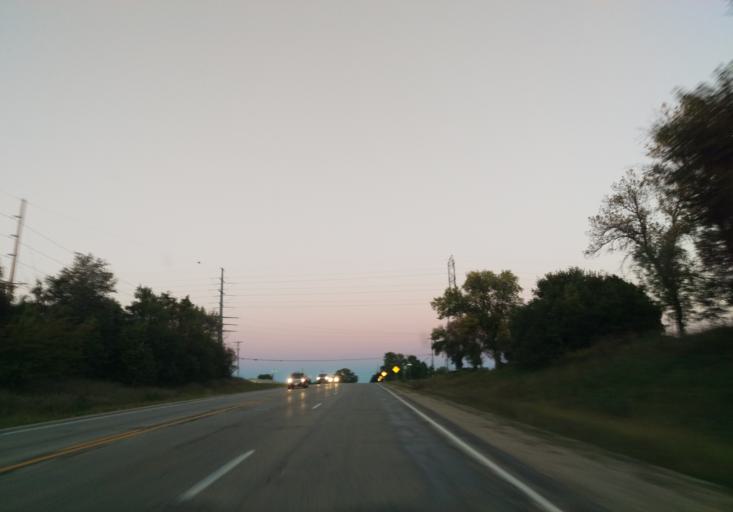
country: US
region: Wisconsin
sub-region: Rock County
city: Janesville
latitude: 42.7302
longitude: -89.0498
